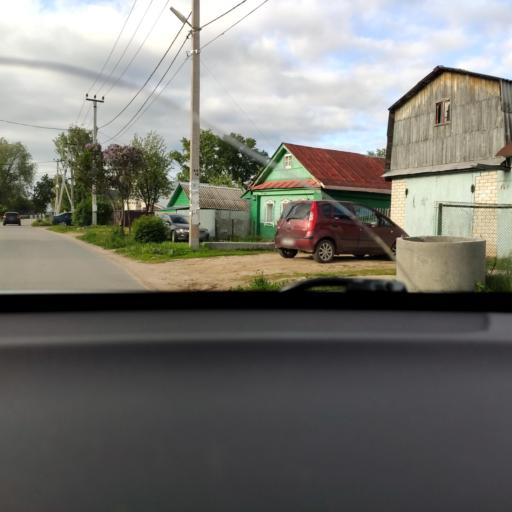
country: RU
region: Tatarstan
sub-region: Gorod Kazan'
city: Kazan
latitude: 55.8792
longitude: 49.0842
